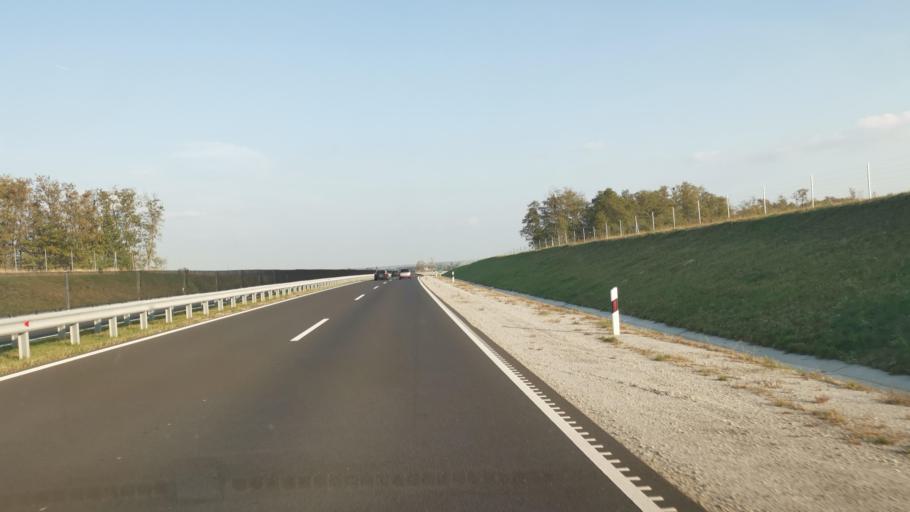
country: HU
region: Gyor-Moson-Sopron
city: Nagycenk
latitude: 47.5810
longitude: 16.7507
